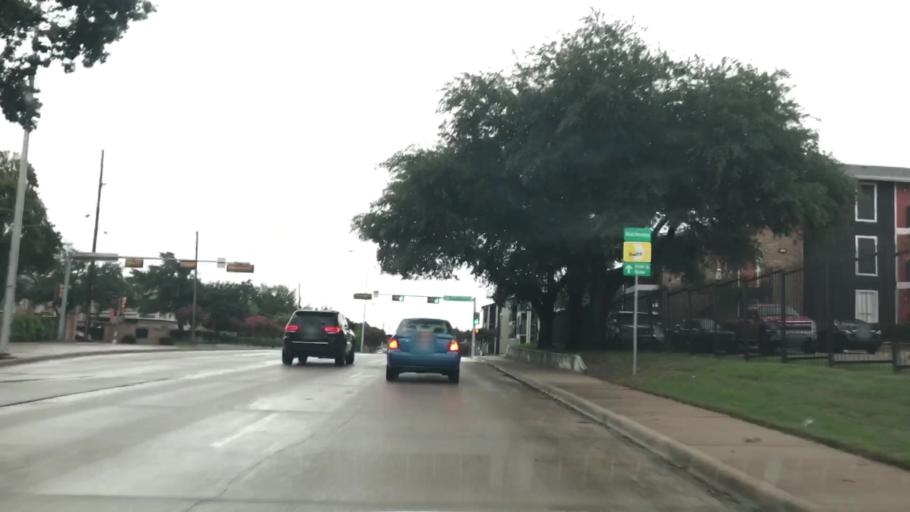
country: US
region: Texas
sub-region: Dallas County
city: Richardson
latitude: 32.8944
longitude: -96.7292
